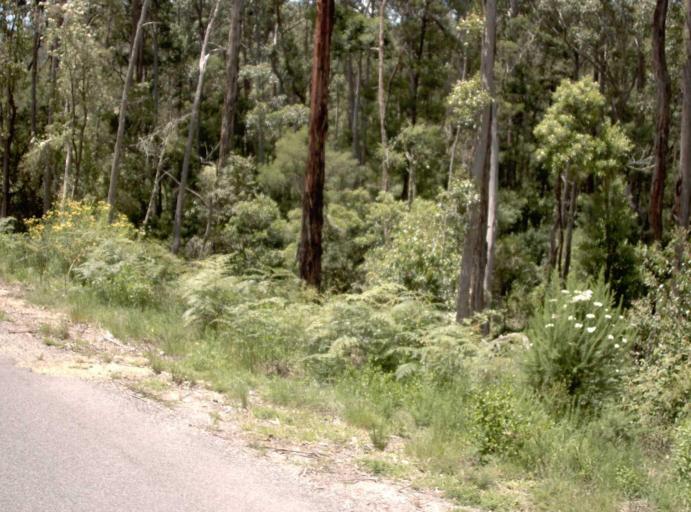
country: AU
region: New South Wales
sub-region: Bombala
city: Bombala
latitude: -37.5261
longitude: 148.9319
